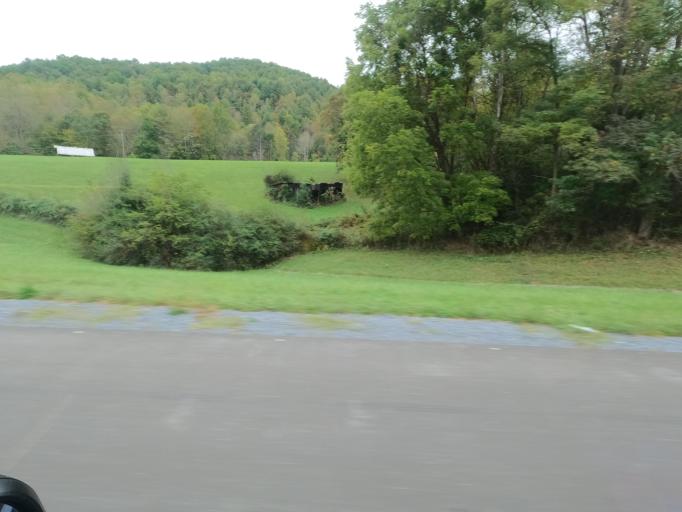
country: US
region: Tennessee
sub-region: Unicoi County
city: Unicoi
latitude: 36.1934
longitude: -82.3697
